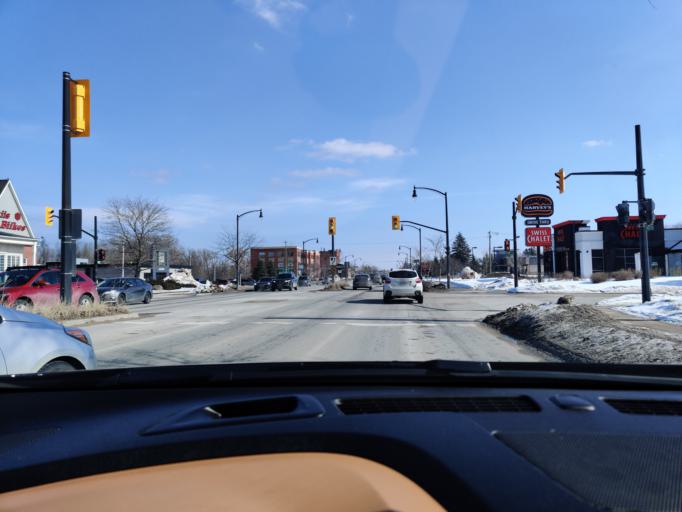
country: CA
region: Ontario
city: Collingwood
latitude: 44.5014
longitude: -80.2314
